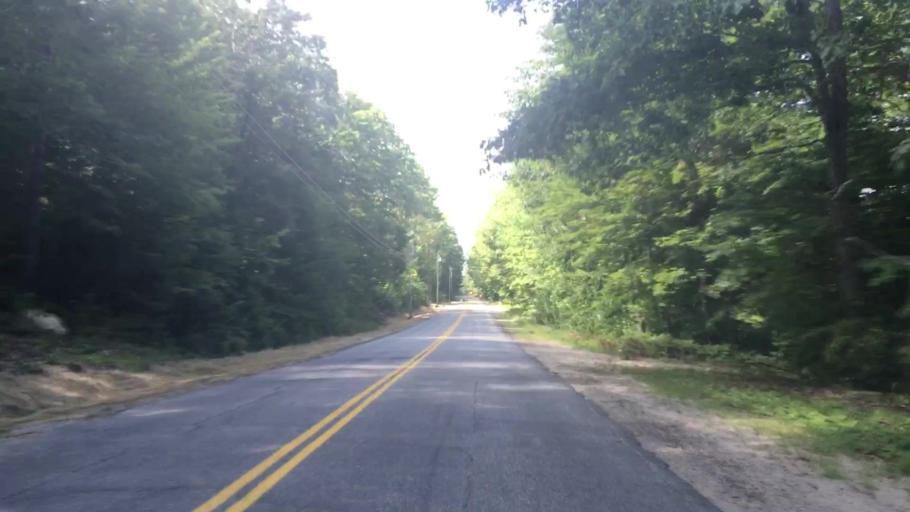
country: US
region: Maine
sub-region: Androscoggin County
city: Poland
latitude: 44.0196
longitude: -70.4236
